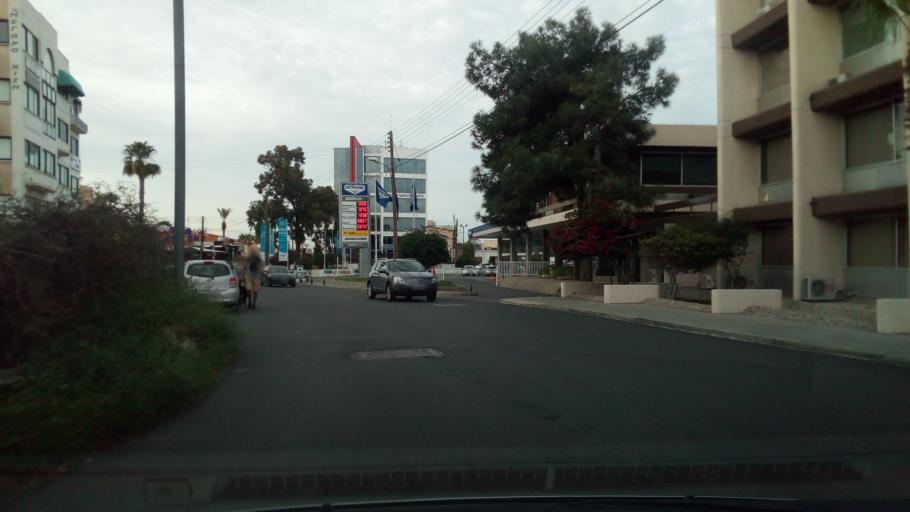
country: CY
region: Larnaka
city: Larnaca
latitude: 34.9221
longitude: 33.6335
